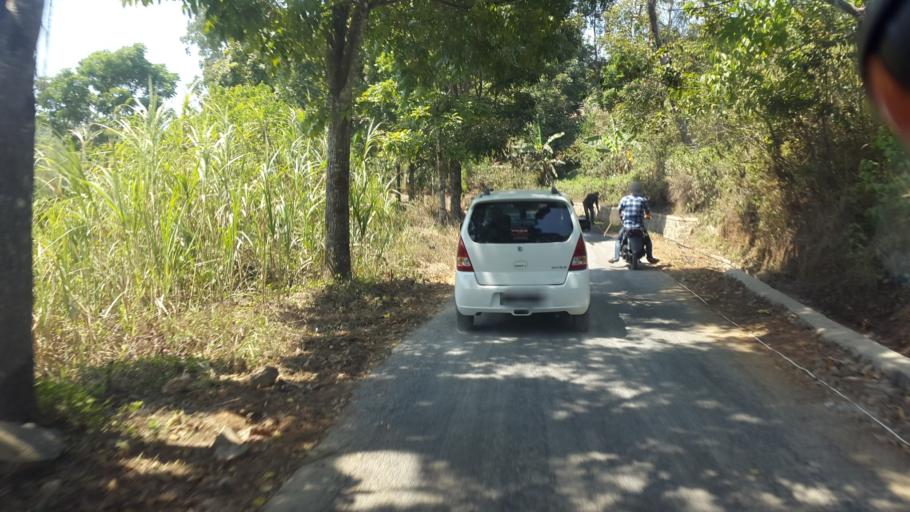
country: ID
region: West Java
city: Ciemas Satu
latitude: -7.1462
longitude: 106.5443
